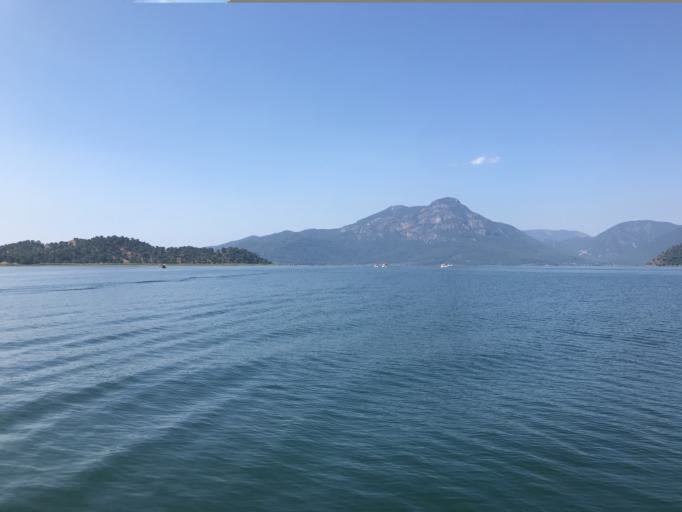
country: TR
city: Dalyan
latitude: 36.9096
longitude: 28.6523
